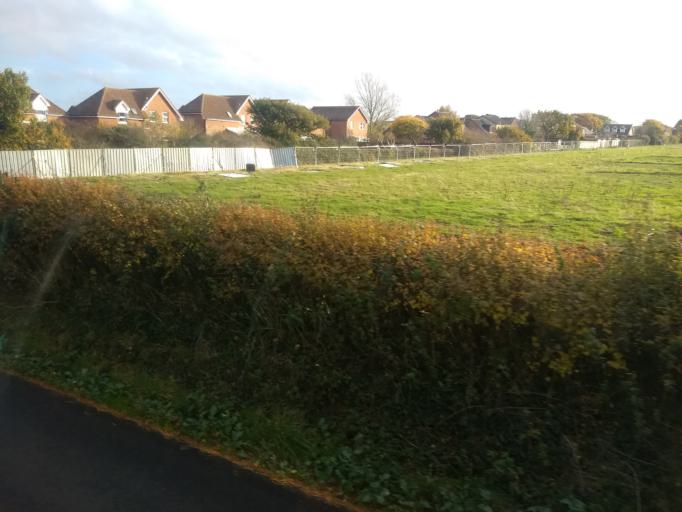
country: GB
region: England
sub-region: Isle of Wight
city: Shalfleet
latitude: 50.7017
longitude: -1.4221
